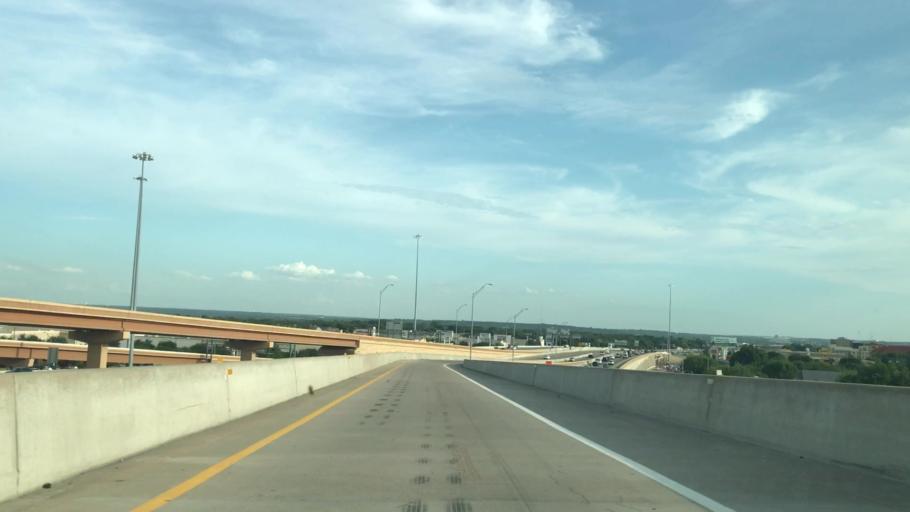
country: US
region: Texas
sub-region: Tarrant County
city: North Richland Hills
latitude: 32.8292
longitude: -97.2061
